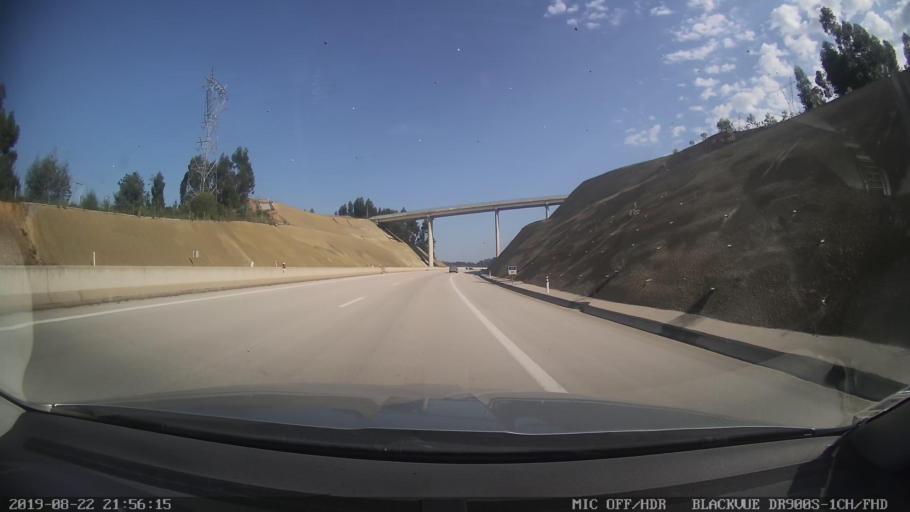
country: PT
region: Coimbra
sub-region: Coimbra
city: Coimbra
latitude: 40.1670
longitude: -8.3783
